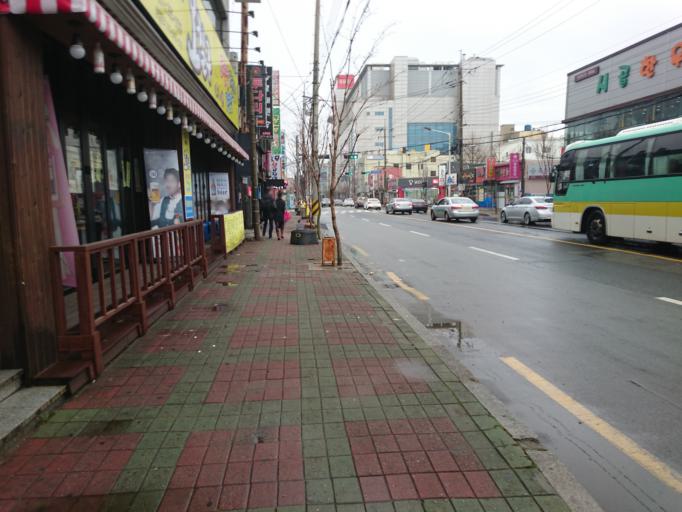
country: KR
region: Gyeongsangbuk-do
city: Enjitsu
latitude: 36.0142
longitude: 129.3471
